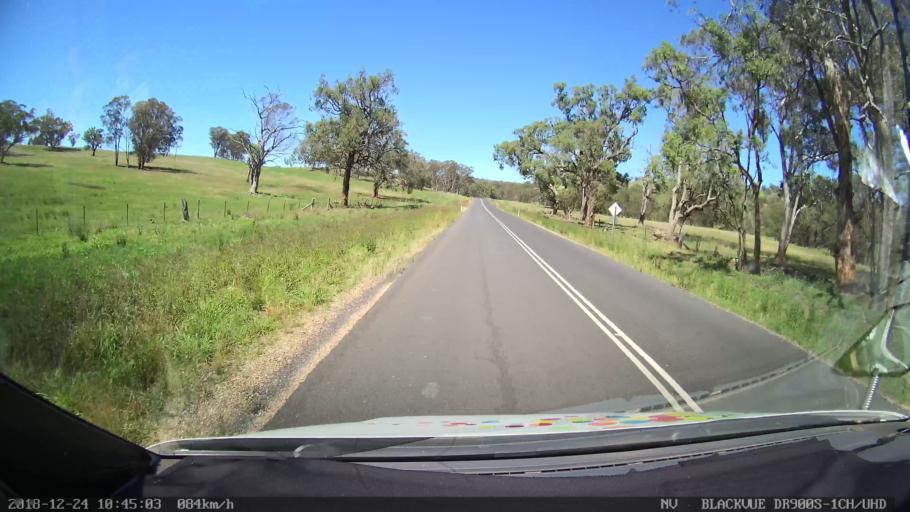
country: AU
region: New South Wales
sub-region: Upper Hunter Shire
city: Merriwa
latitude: -31.8990
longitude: 150.4391
